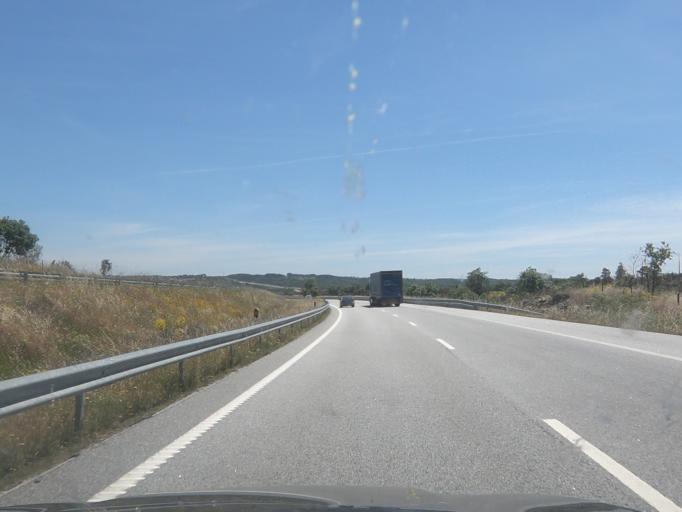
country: PT
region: Guarda
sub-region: Pinhel
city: Pinhel
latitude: 40.6032
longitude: -7.0476
